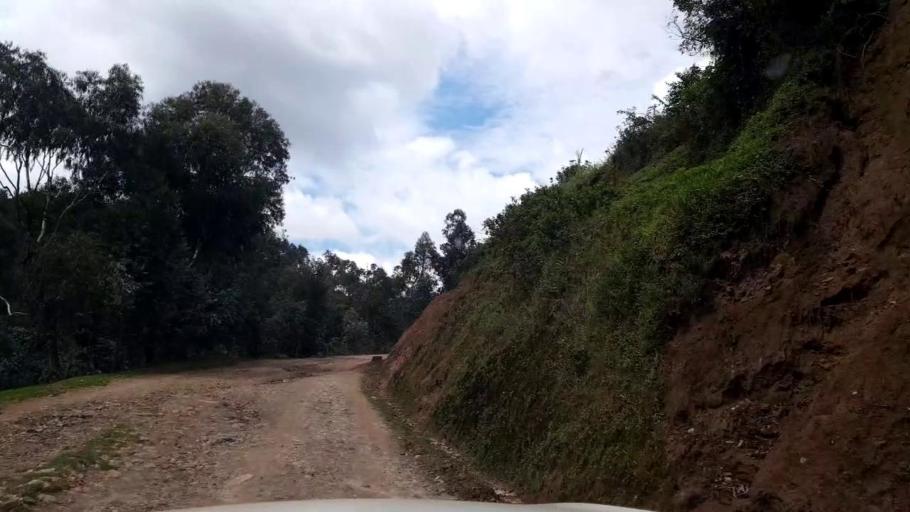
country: RW
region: Western Province
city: Kibuye
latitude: -1.9044
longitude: 29.4540
